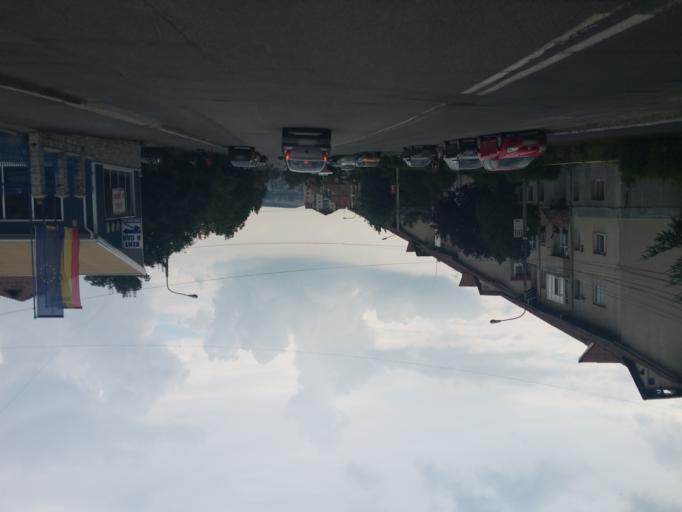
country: RO
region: Salaj
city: Zalau
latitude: 47.1688
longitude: 23.0699
